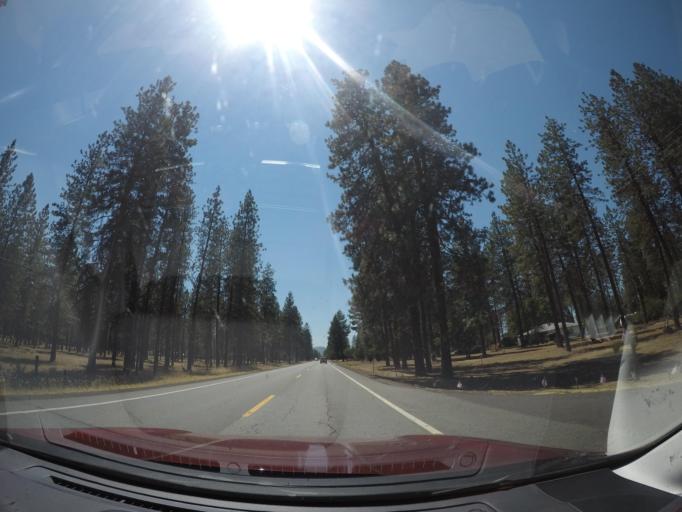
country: US
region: California
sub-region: Shasta County
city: Burney
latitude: 41.0613
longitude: -121.3682
